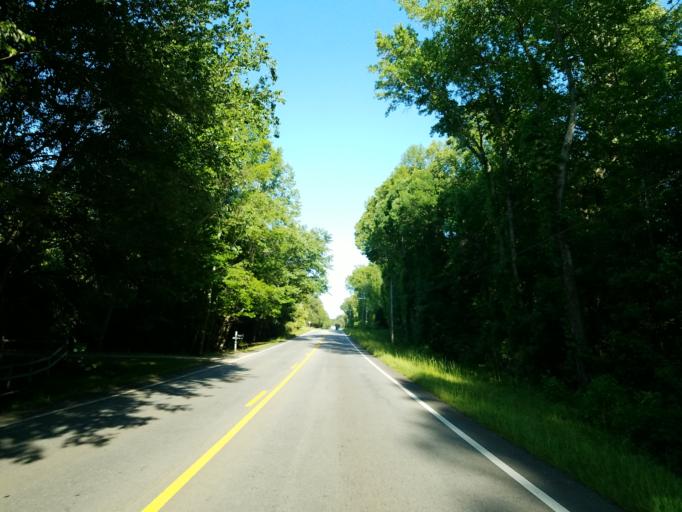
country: US
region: Georgia
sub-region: Carroll County
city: Villa Rica
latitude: 33.7334
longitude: -84.8495
